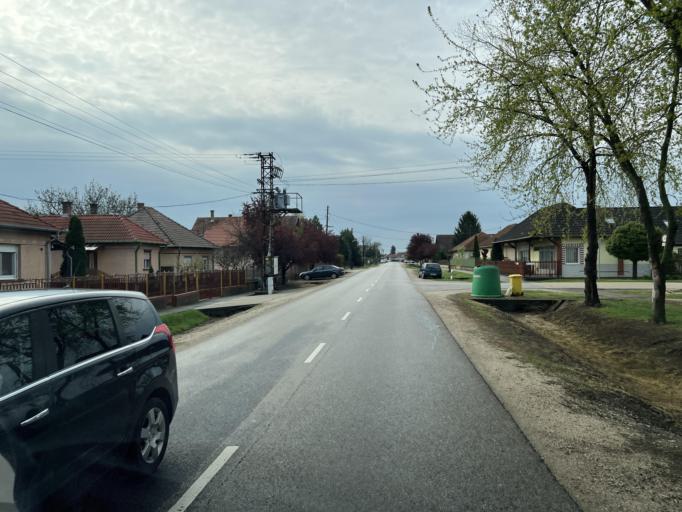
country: HU
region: Pest
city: Nyaregyhaza
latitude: 47.2337
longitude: 19.4471
